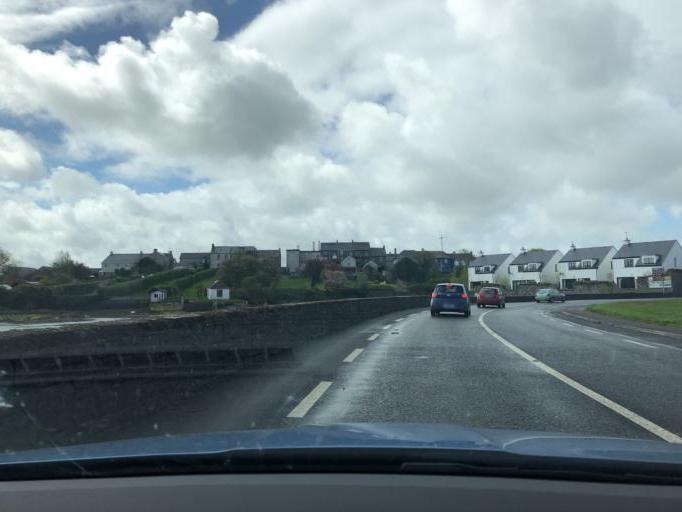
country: IE
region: Munster
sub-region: An Clar
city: Kilrush
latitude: 52.5747
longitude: -9.3738
